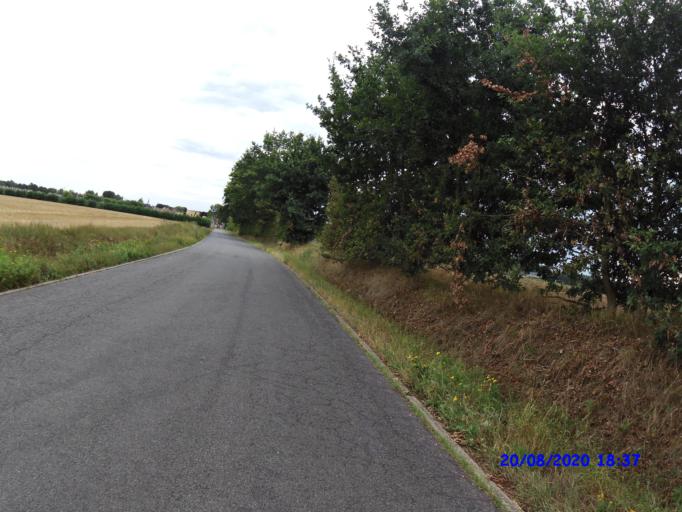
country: BE
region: Flanders
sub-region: Provincie Limburg
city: Sint-Truiden
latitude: 50.8344
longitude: 5.1761
